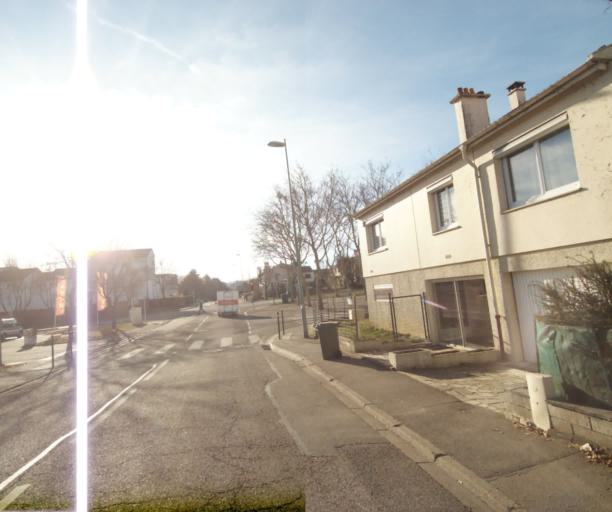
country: FR
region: Lorraine
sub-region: Departement de Meurthe-et-Moselle
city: Chavigny
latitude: 48.6575
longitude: 6.1114
